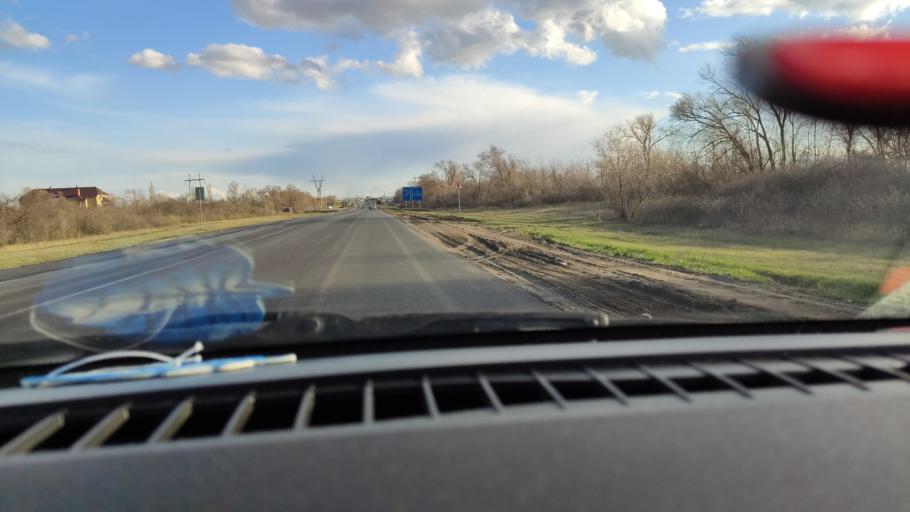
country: RU
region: Saratov
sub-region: Saratovskiy Rayon
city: Saratov
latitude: 51.6742
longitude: 46.0006
